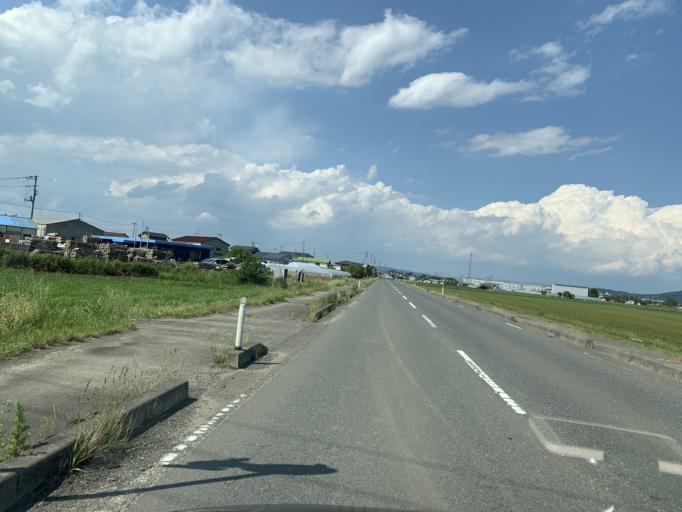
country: JP
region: Miyagi
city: Wakuya
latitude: 38.4649
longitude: 141.1286
